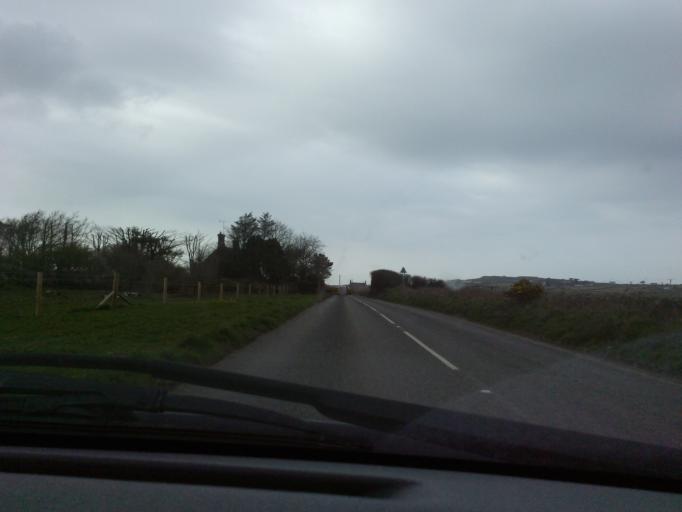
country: GB
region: England
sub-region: Cornwall
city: Saint Just
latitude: 50.1063
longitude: -5.6713
